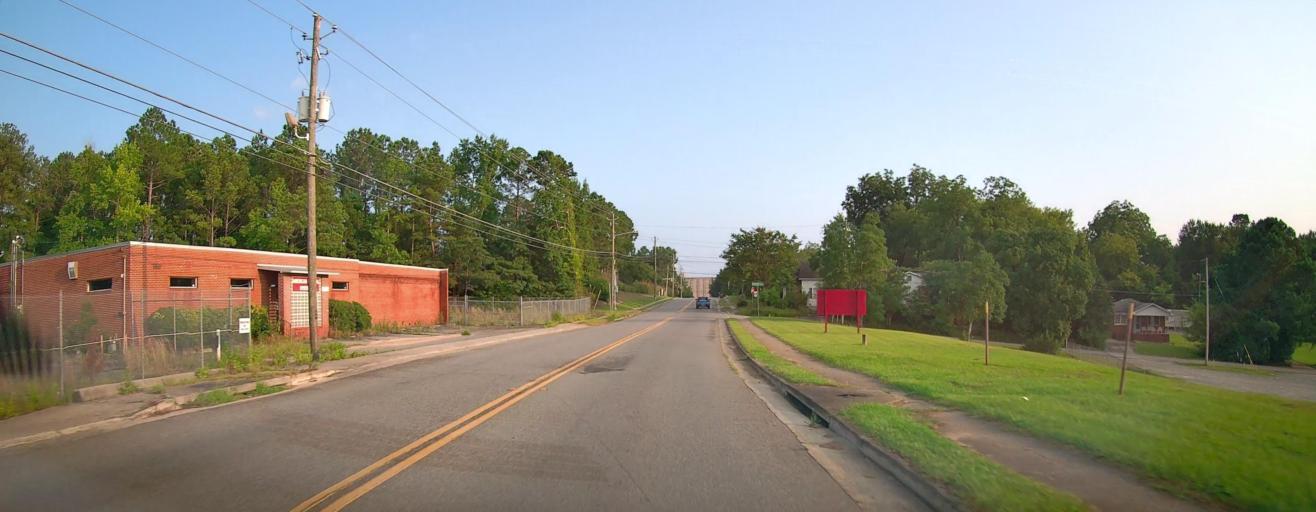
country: US
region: Georgia
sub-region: Bibb County
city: Macon
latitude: 32.8647
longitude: -83.6177
